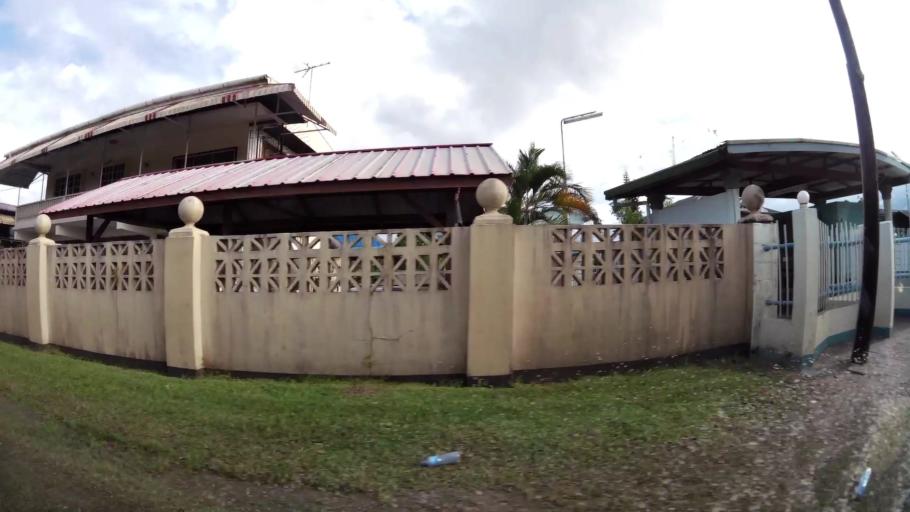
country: SR
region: Paramaribo
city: Paramaribo
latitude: 5.8474
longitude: -55.2396
